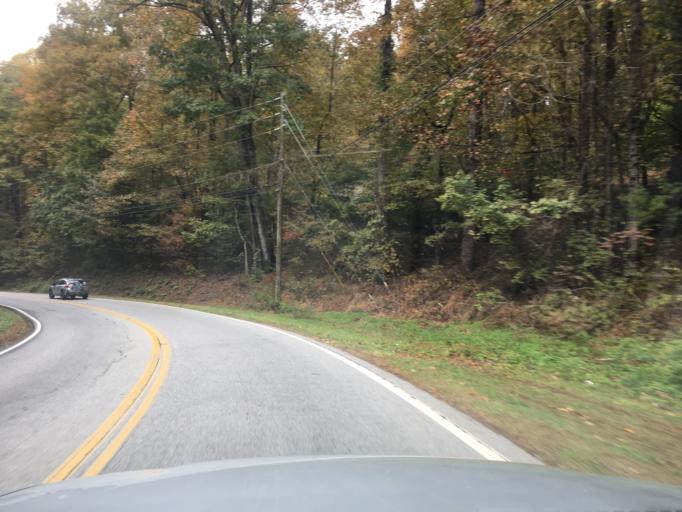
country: US
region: North Carolina
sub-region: Henderson County
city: Flat Rock
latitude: 35.2507
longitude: -82.4276
